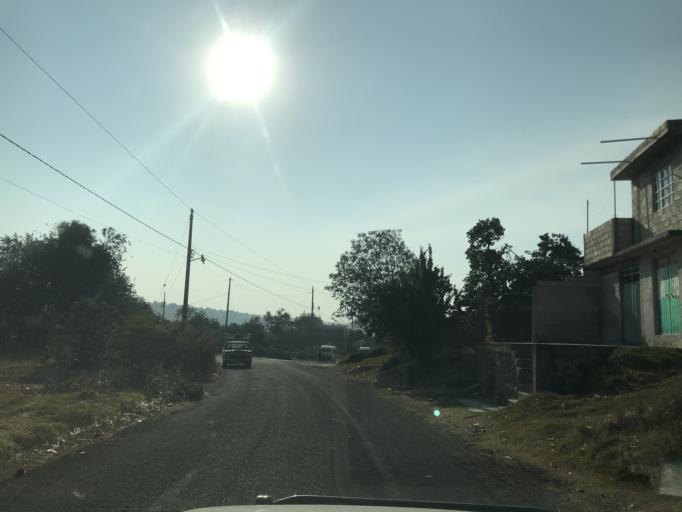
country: MX
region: Puebla
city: San Nicolas de los Ranchos
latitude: 19.0837
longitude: -98.5226
